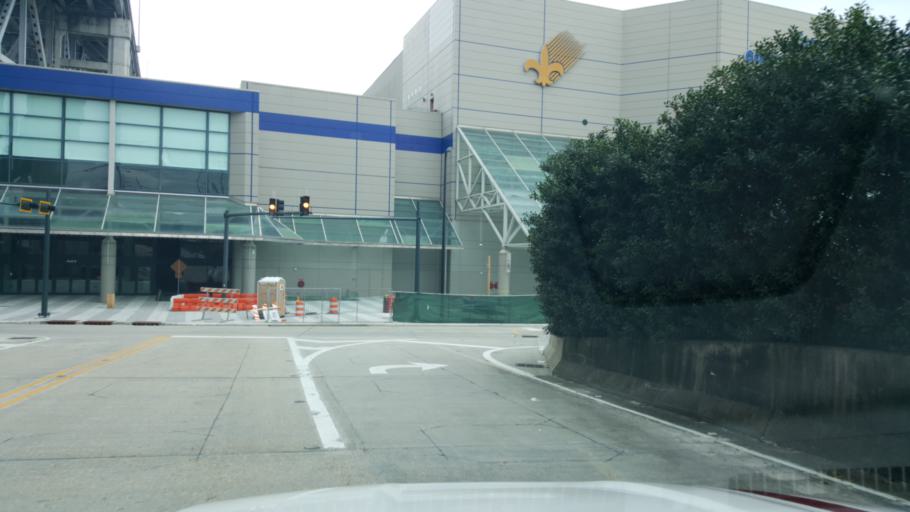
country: US
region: Louisiana
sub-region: Orleans Parish
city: New Orleans
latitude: 29.9375
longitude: -90.0646
